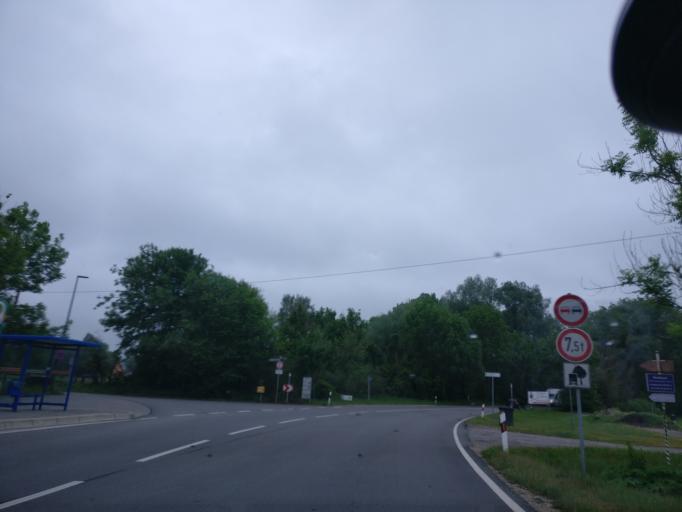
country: DE
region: Bavaria
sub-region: Upper Bavaria
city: Dachau
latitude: 48.2282
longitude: 11.4284
